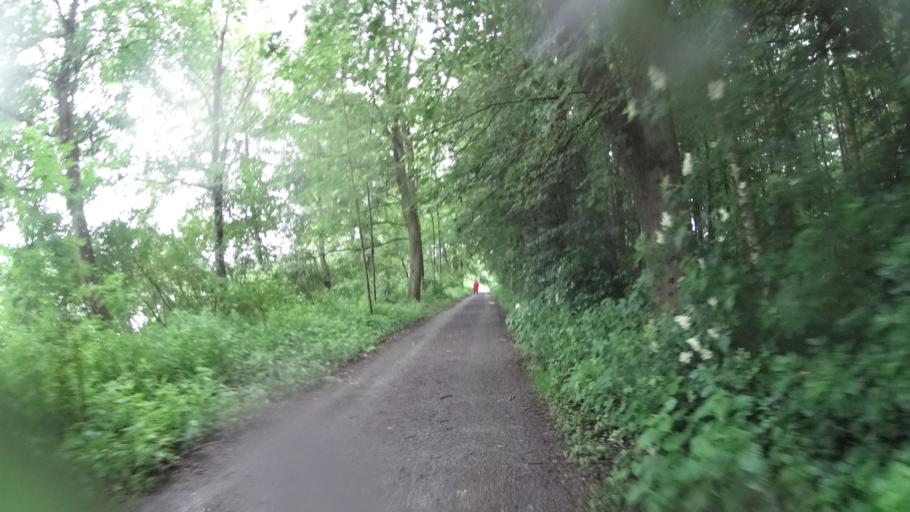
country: AT
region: Upper Austria
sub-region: Politischer Bezirk Scharding
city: Scharding
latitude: 48.4687
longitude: 13.4281
